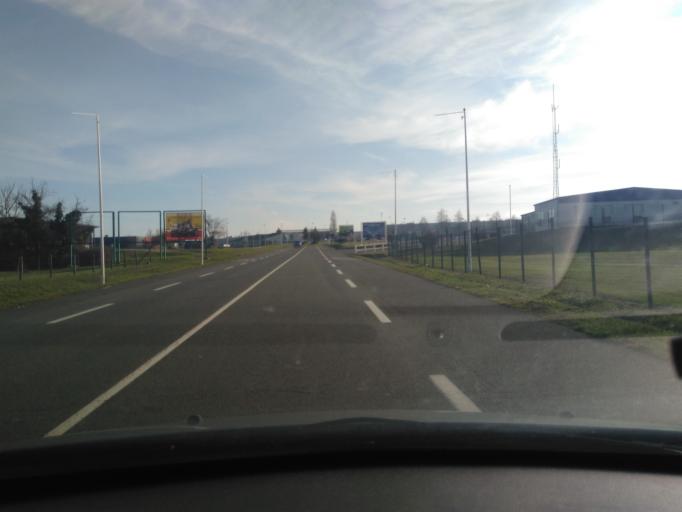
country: FR
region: Bourgogne
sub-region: Departement de la Nievre
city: Magny-Cours
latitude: 46.8688
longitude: 3.1578
